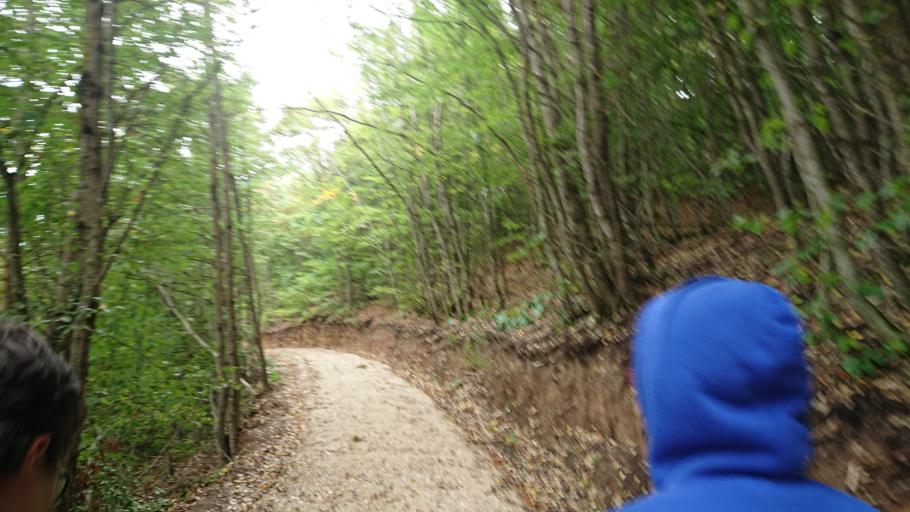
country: TR
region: Bilecik
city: Pazaryeri
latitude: 40.0159
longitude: 29.7939
